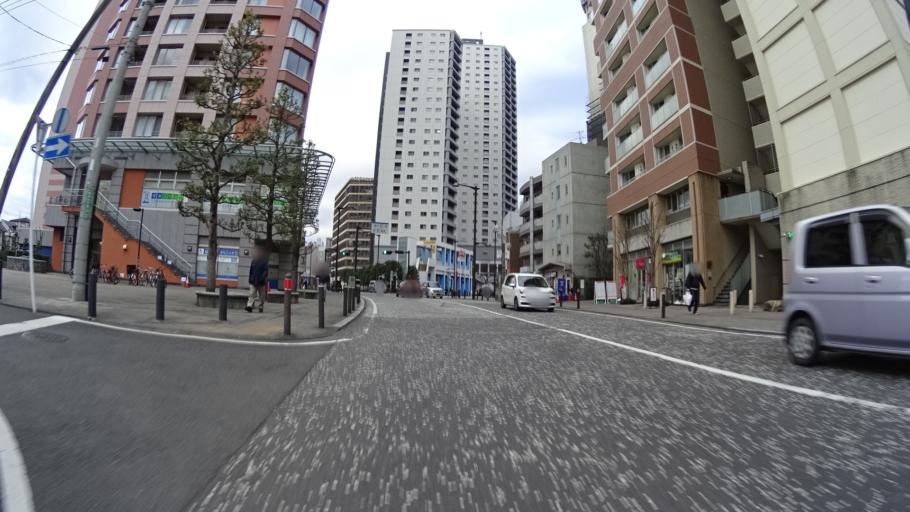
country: JP
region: Tokyo
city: Hachioji
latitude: 35.5972
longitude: 139.3424
